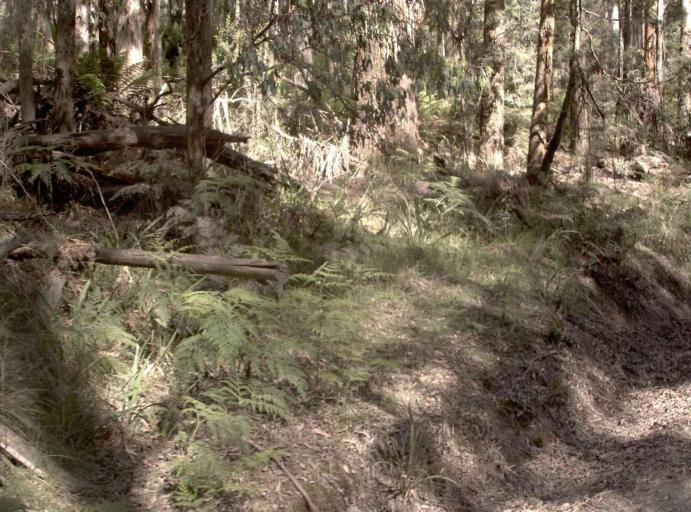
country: AU
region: New South Wales
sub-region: Bombala
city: Bombala
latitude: -37.2384
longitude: 148.7563
